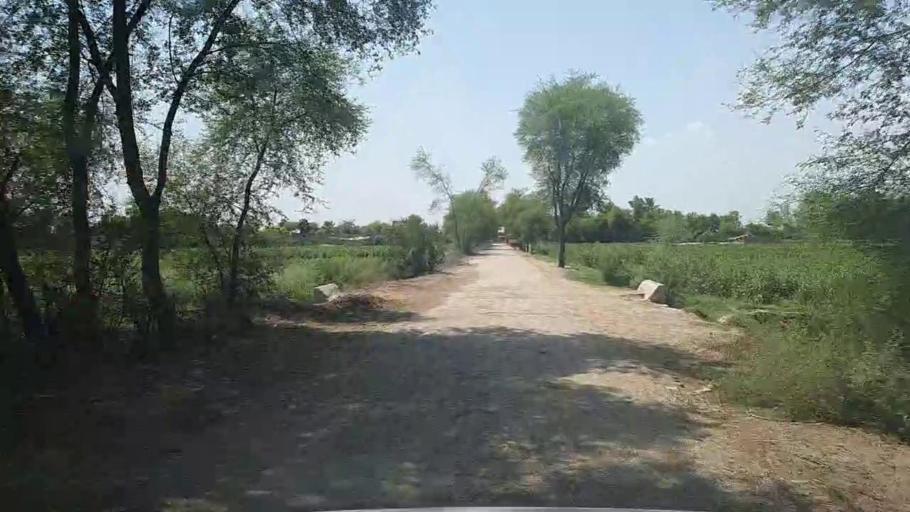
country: PK
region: Sindh
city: Ubauro
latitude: 28.1790
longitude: 69.7068
